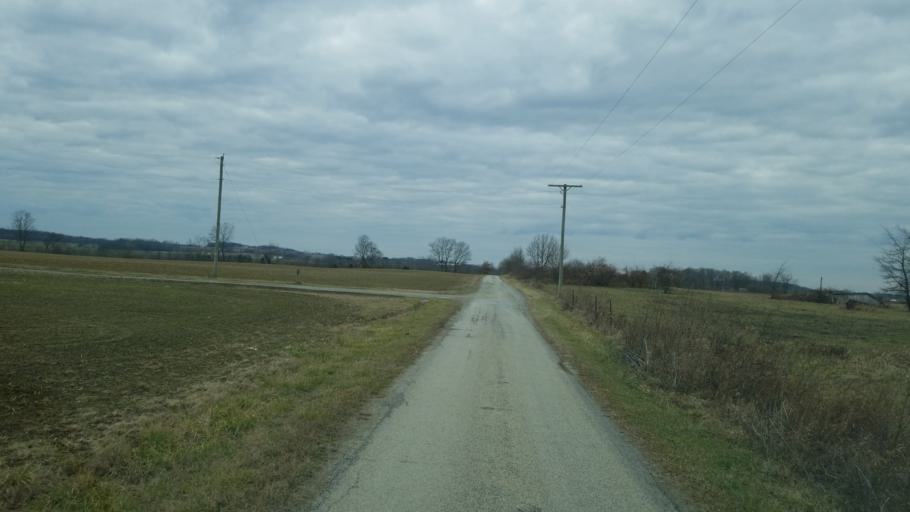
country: US
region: Ohio
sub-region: Highland County
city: Greenfield
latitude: 39.3206
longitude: -83.3373
